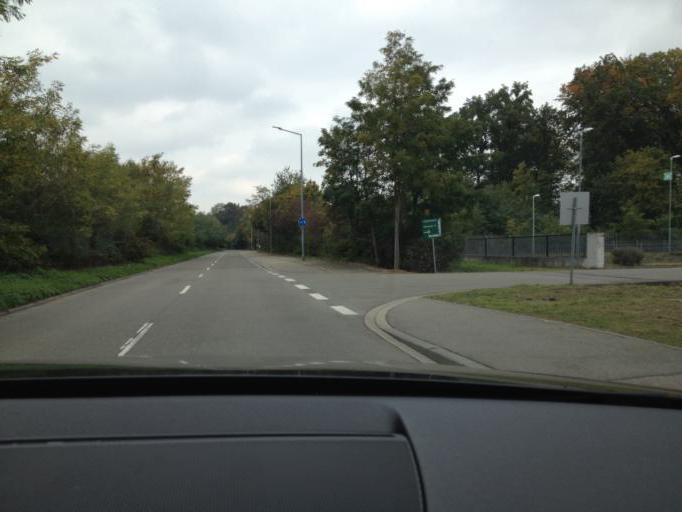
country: DE
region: Rheinland-Pfalz
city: Speyer
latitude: 49.3372
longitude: 8.4151
